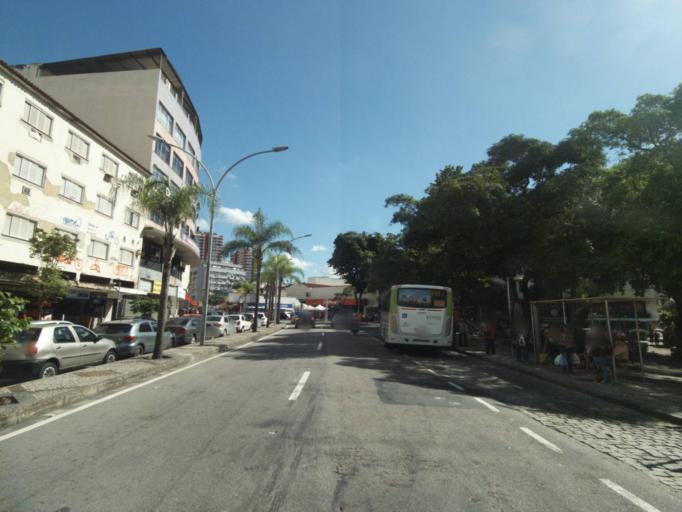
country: BR
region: Rio de Janeiro
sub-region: Rio De Janeiro
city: Rio de Janeiro
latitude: -22.9019
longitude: -43.2794
